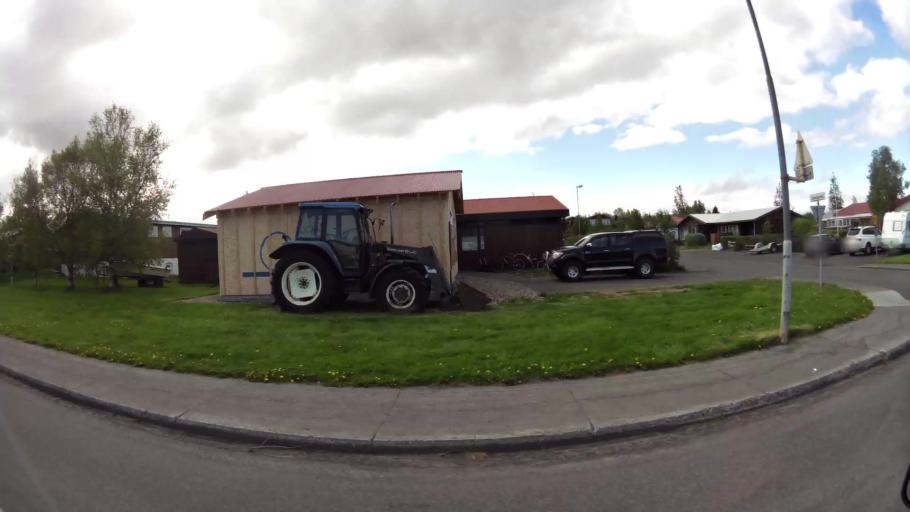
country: IS
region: East
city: Egilsstadir
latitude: 65.2667
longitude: -14.3849
